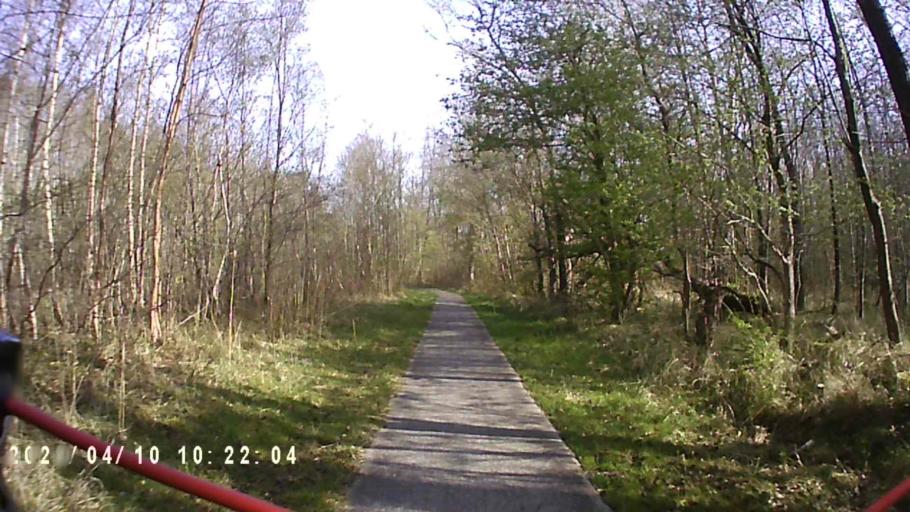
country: NL
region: Friesland
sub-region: Gemeente Dongeradeel
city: Anjum
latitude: 53.3823
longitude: 6.2158
